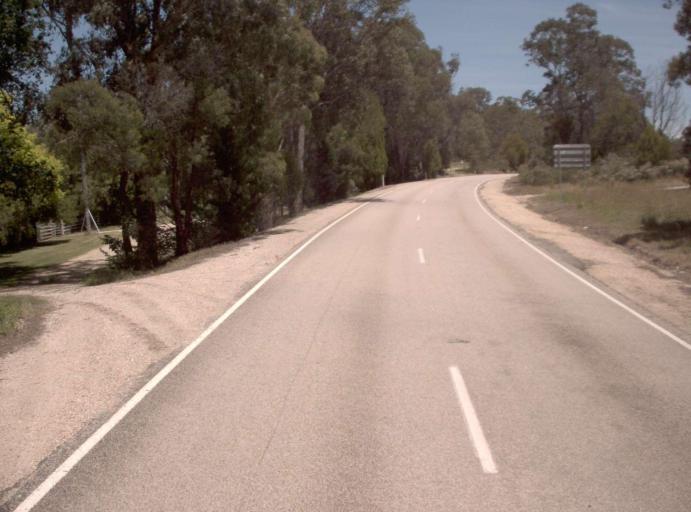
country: AU
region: Victoria
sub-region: East Gippsland
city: Lakes Entrance
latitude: -37.6712
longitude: 147.8674
